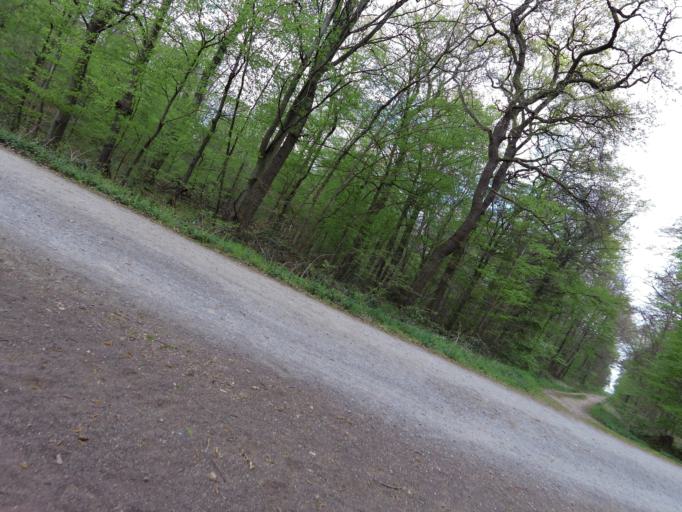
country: DE
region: North Rhine-Westphalia
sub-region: Regierungsbezirk Koln
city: Wachtberg
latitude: 50.6747
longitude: 7.0588
